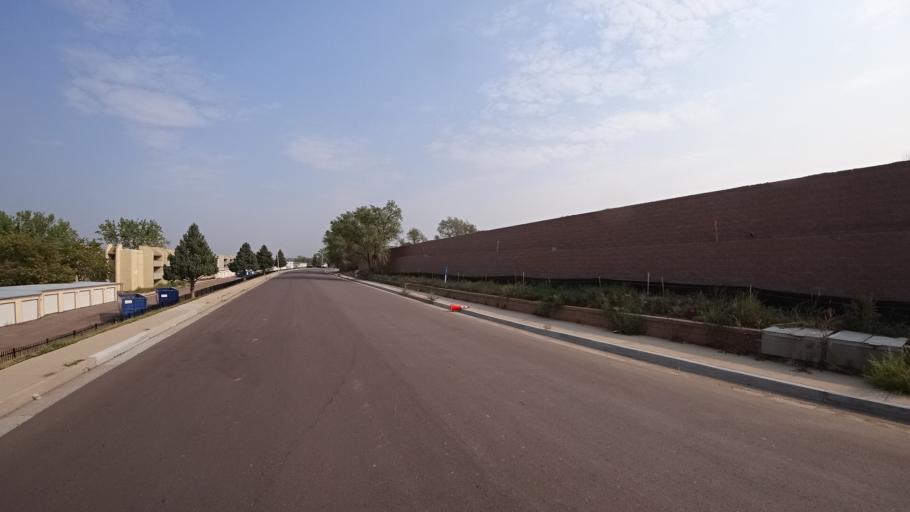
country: US
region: Colorado
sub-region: El Paso County
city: Stratmoor
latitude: 38.8179
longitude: -104.7535
